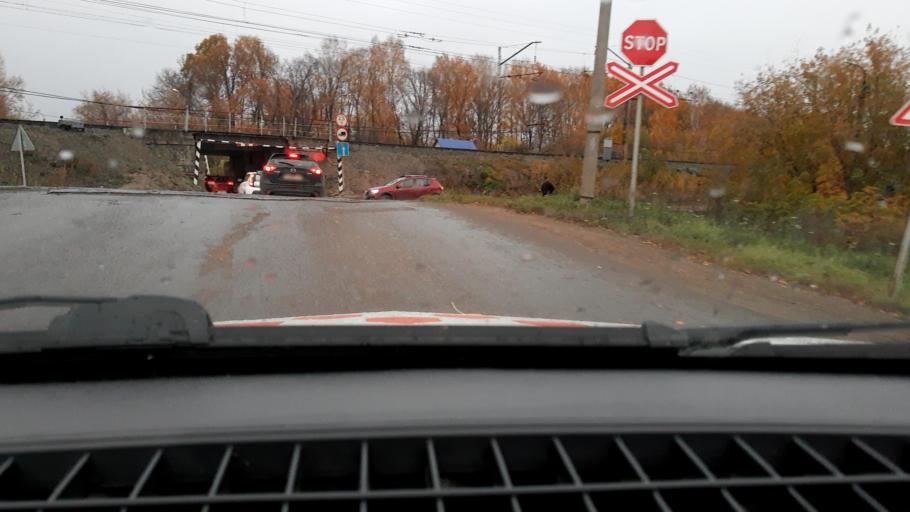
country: RU
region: Bashkortostan
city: Iglino
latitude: 54.7760
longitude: 56.2290
